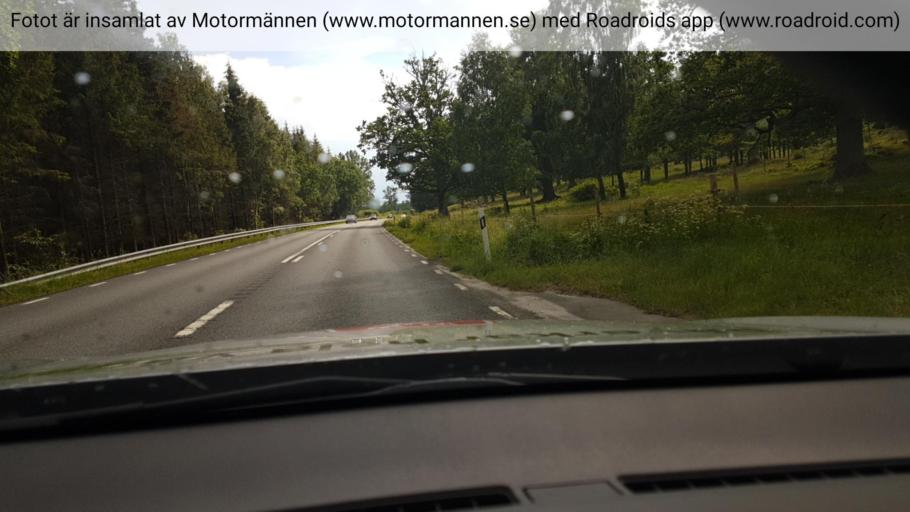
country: SE
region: Vaestra Goetaland
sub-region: Hjo Kommun
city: Hjo
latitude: 58.1249
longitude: 14.2175
